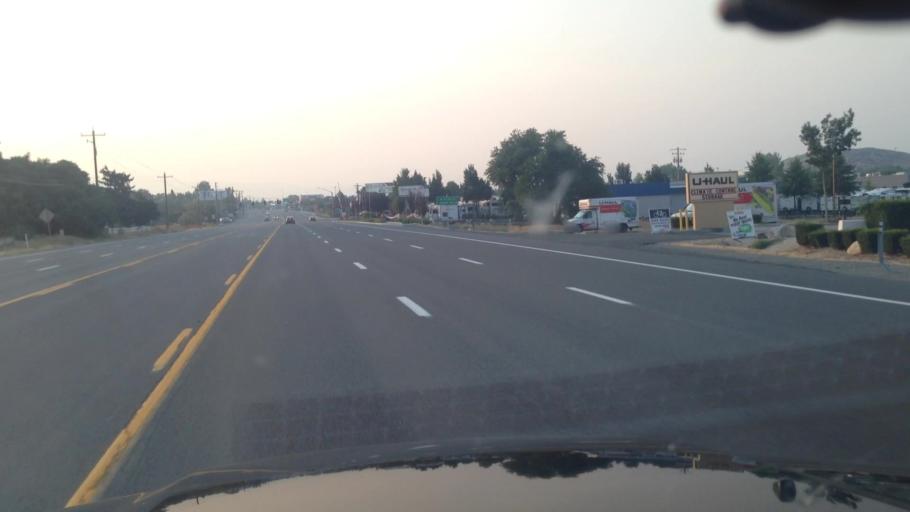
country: US
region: Nevada
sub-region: Washoe County
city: Sparks
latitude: 39.4367
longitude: -119.7680
